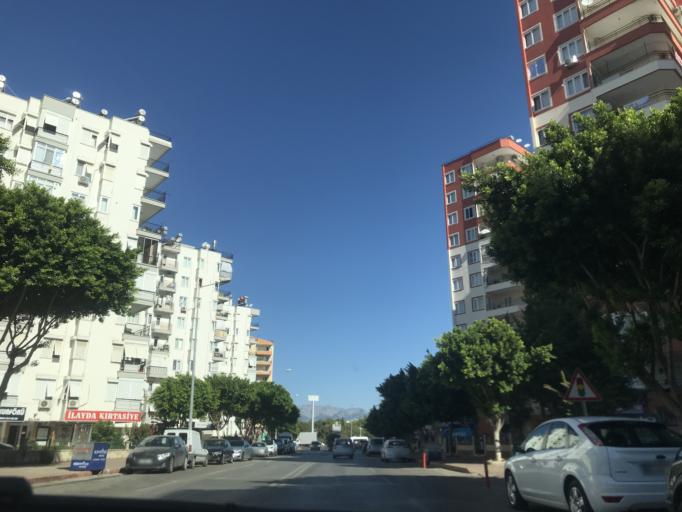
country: TR
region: Antalya
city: Antalya
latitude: 36.8941
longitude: 30.6296
